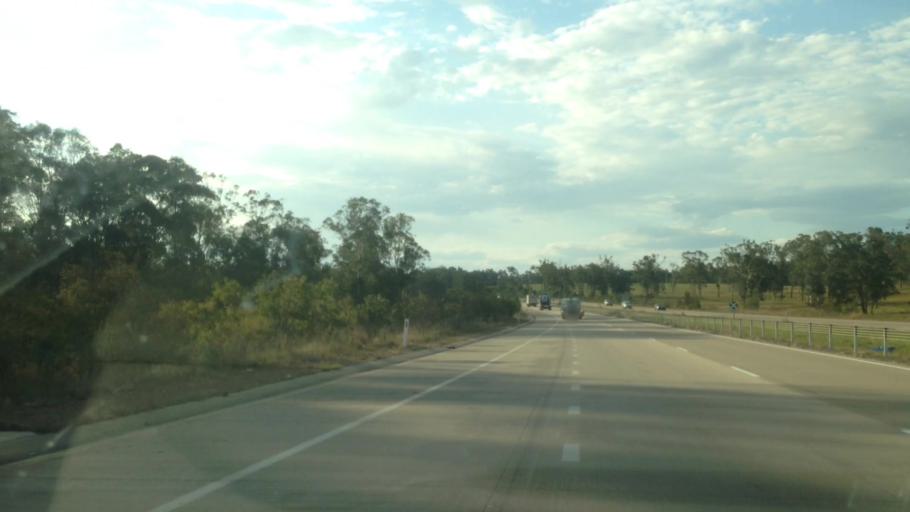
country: AU
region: New South Wales
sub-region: Cessnock
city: Heddon Greta
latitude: -32.8394
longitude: 151.5409
